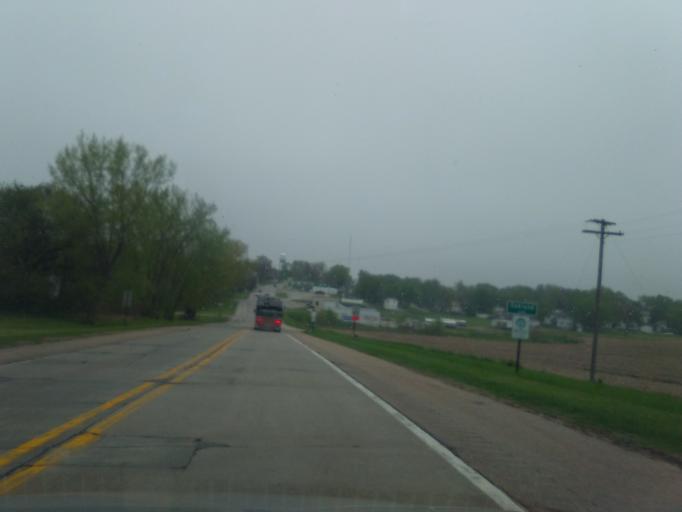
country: US
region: Nebraska
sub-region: Burt County
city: Oakland
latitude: 41.8296
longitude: -96.4628
